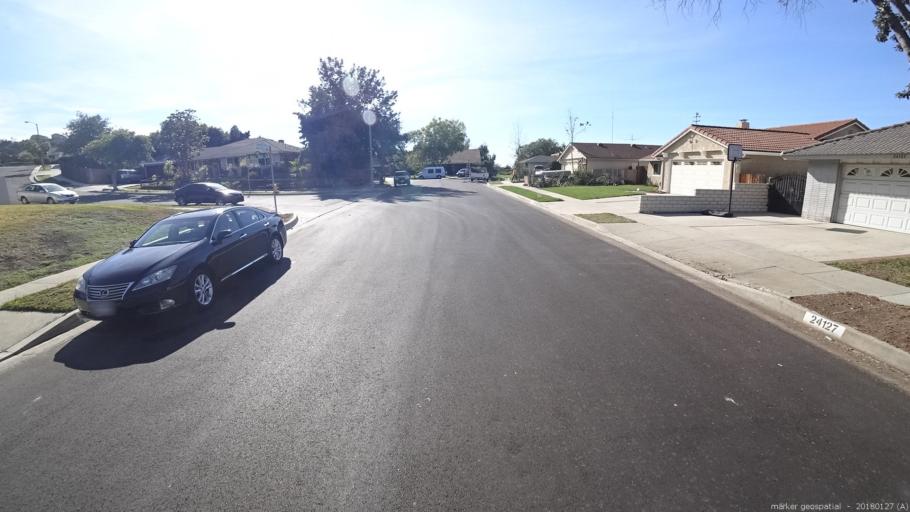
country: US
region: California
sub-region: Los Angeles County
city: Diamond Bar
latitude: 34.0246
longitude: -117.7982
